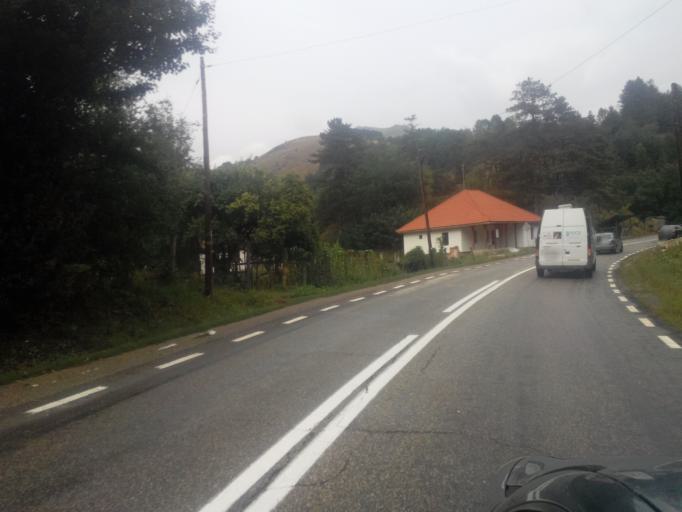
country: RO
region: Alba
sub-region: Comuna Ocolis
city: Ocolis
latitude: 46.4681
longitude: 23.4759
